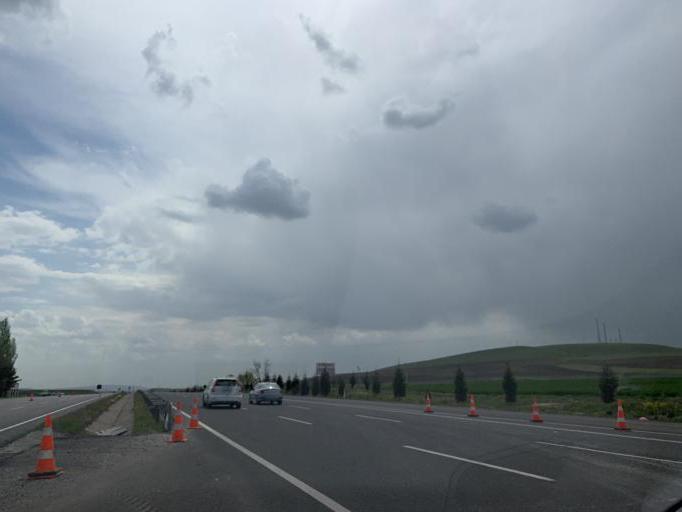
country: TR
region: Ankara
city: Polatli
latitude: 39.6163
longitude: 32.1873
